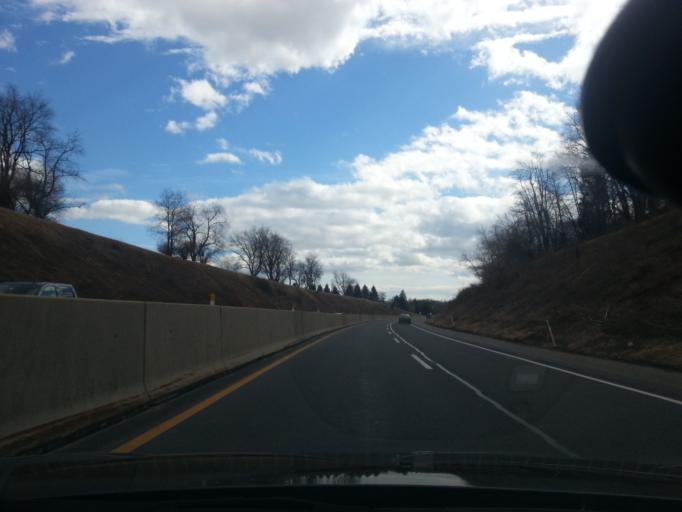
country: US
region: Pennsylvania
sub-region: Lehigh County
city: Schnecksville
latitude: 40.6324
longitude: -75.5773
